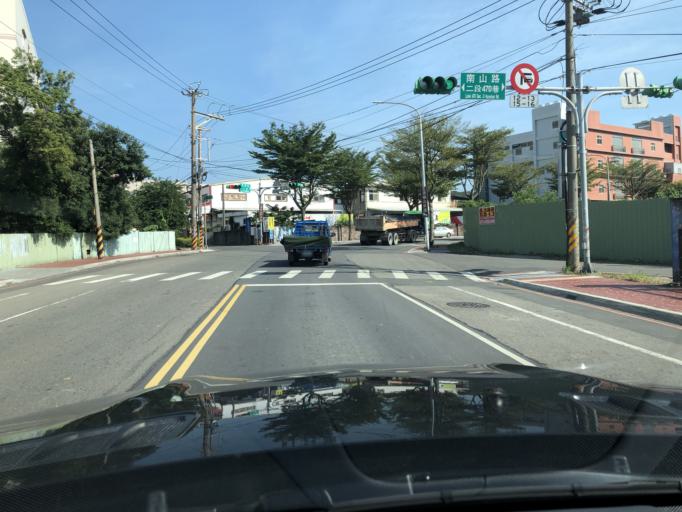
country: TW
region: Taiwan
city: Taoyuan City
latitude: 25.0733
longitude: 121.2868
